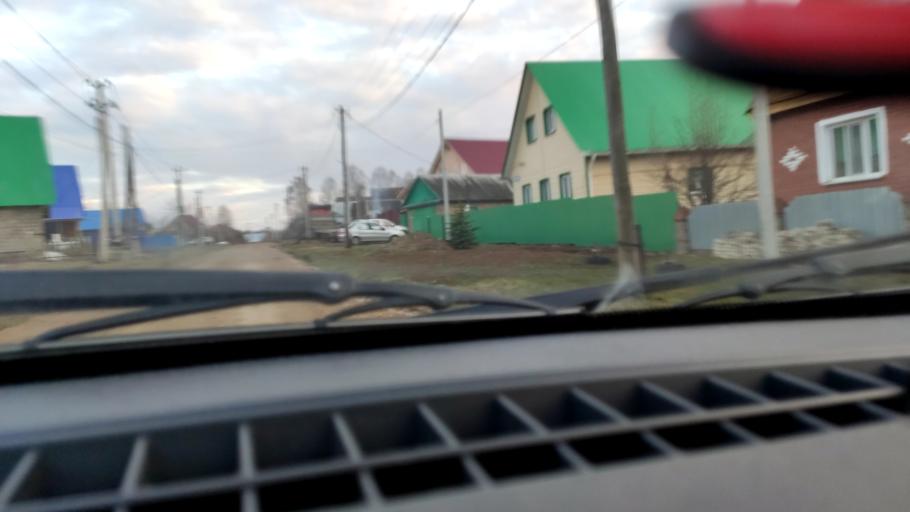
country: RU
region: Bashkortostan
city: Iglino
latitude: 54.8235
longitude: 56.3758
